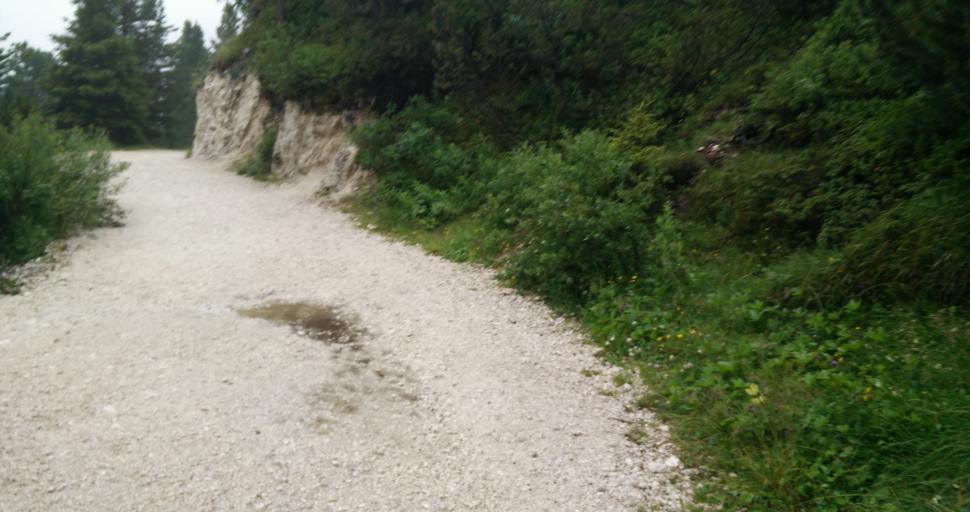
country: IT
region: Trentino-Alto Adige
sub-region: Provincia di Trento
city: Vigo di Fassa
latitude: 46.4462
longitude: 11.6406
